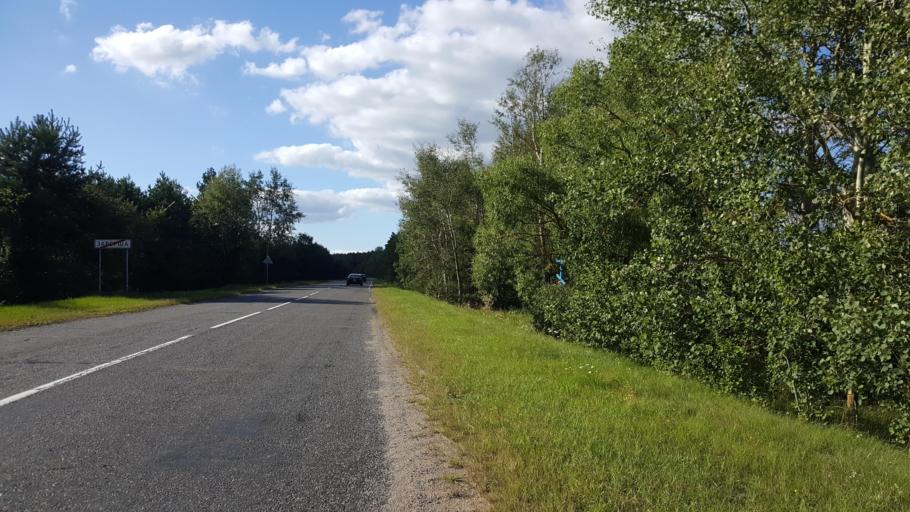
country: BY
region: Brest
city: Zhabinka
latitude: 52.3682
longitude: 24.1412
